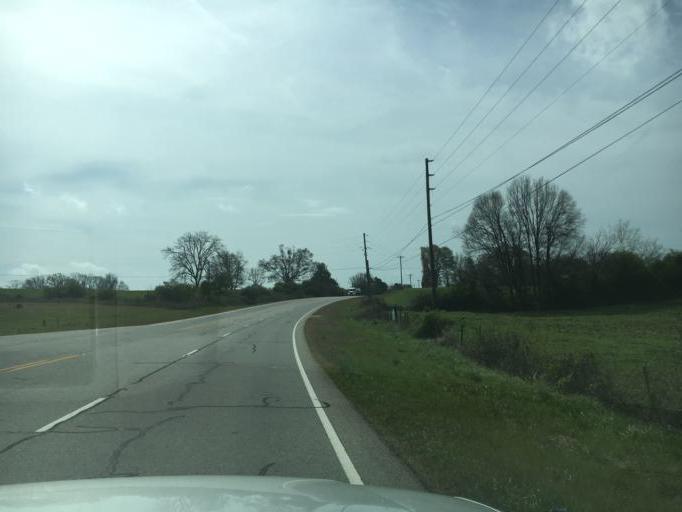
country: US
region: Georgia
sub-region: Franklin County
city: Lavonia
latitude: 34.4501
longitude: -83.0368
